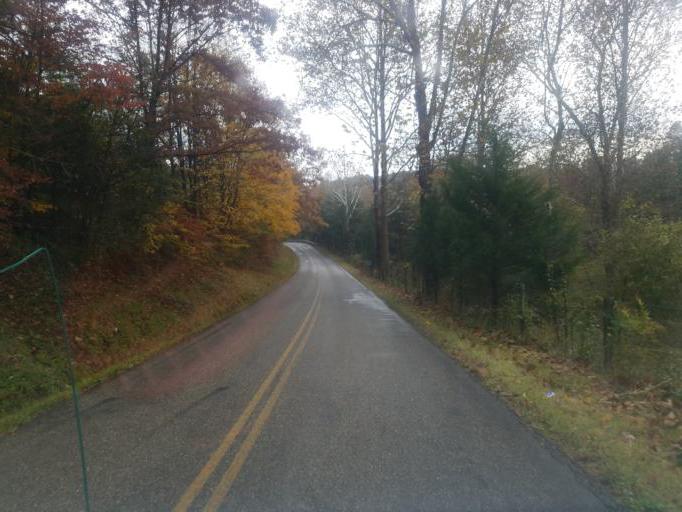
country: US
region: Ohio
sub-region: Washington County
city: Beverly
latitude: 39.5507
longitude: -81.6694
